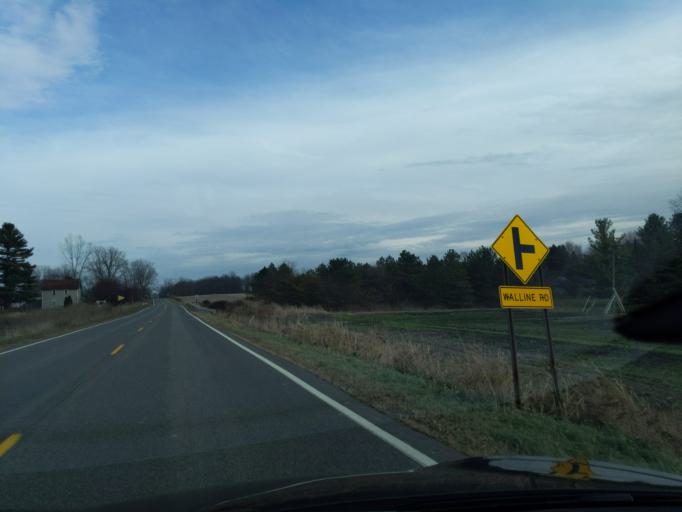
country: US
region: Michigan
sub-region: Ingham County
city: Mason
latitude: 42.6400
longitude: -84.4052
